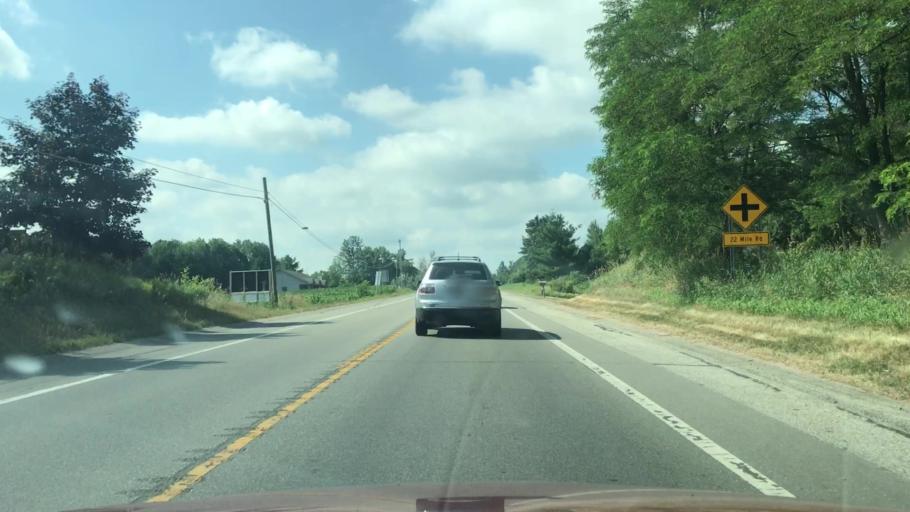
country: US
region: Michigan
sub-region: Kent County
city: Kent City
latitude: 43.2946
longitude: -85.8107
